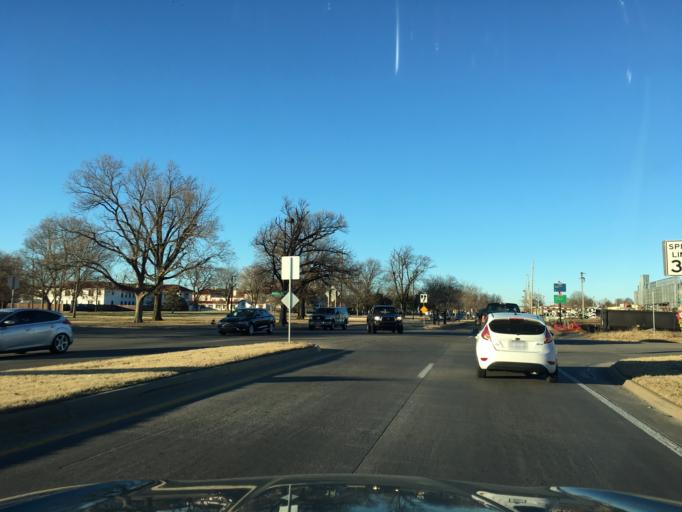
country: US
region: Kansas
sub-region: Sedgwick County
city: Wichita
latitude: 37.6776
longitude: -97.3529
